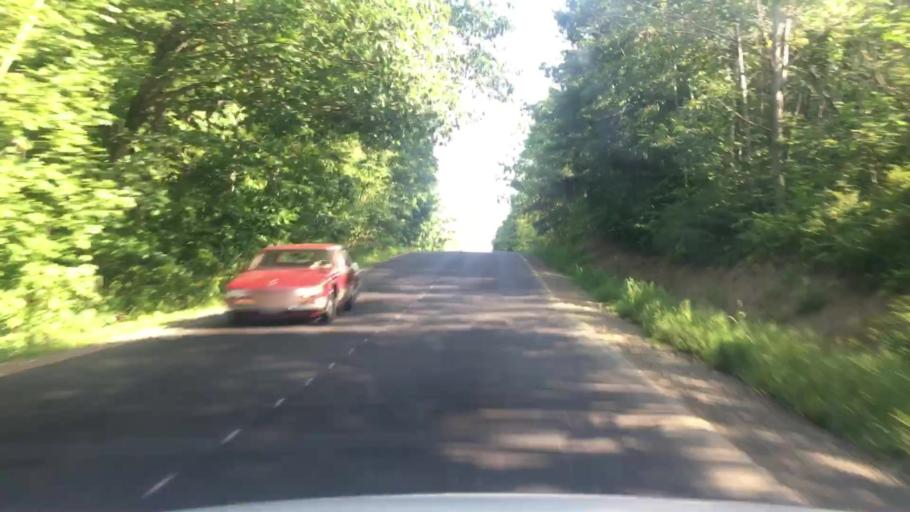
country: US
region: Maine
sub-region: Kennebec County
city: Waterville
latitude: 44.5742
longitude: -69.6583
